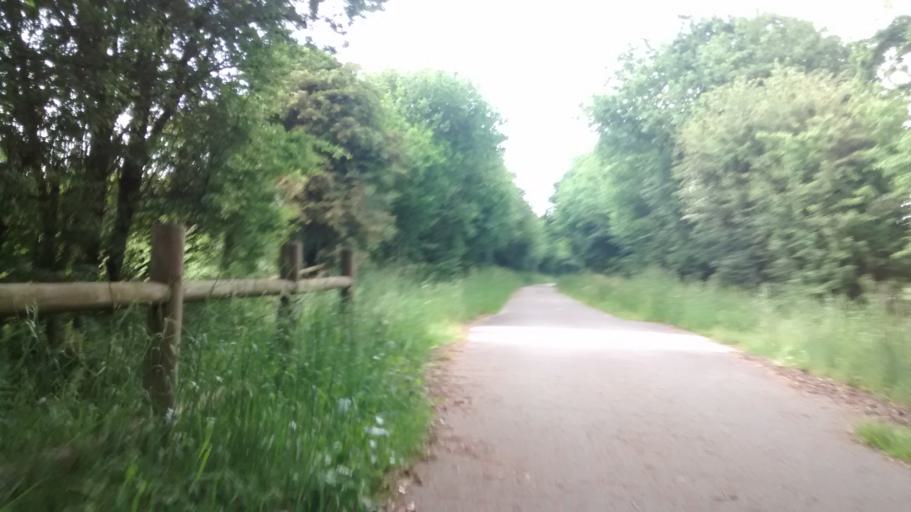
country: FR
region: Brittany
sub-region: Departement du Morbihan
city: Molac
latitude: 47.7197
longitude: -2.4225
